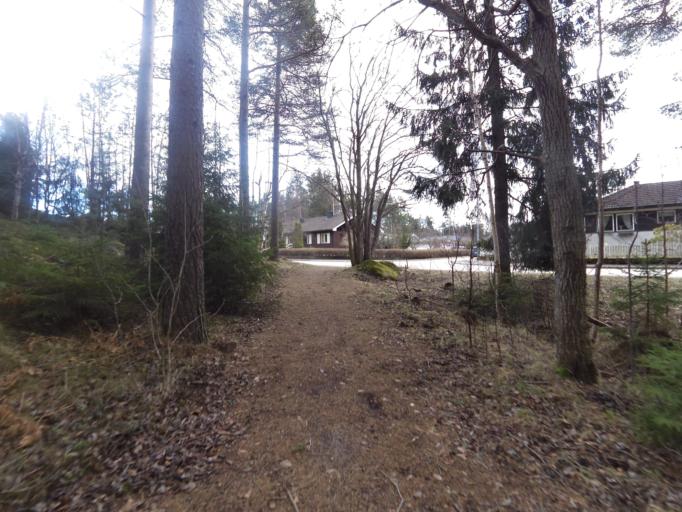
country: SE
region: Gaevleborg
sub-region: Gavle Kommun
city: Gavle
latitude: 60.6881
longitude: 17.0936
